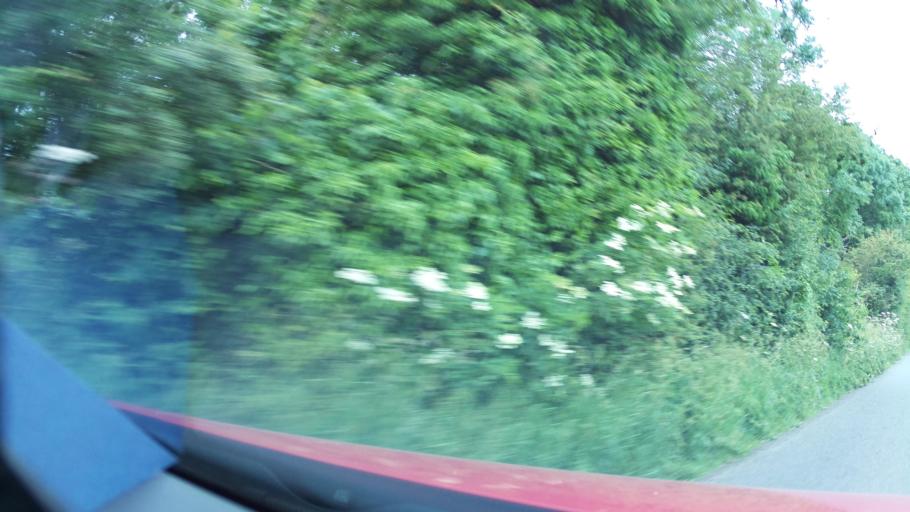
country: GB
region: England
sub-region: District of Rutland
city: Langham
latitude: 52.6800
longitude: -0.8151
